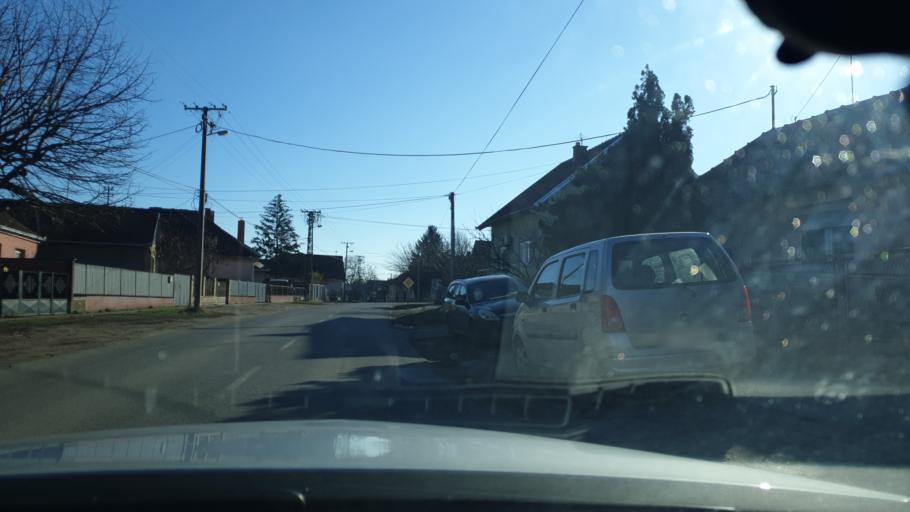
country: RS
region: Autonomna Pokrajina Vojvodina
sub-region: Sremski Okrug
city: Ruma
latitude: 45.0131
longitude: 19.8165
